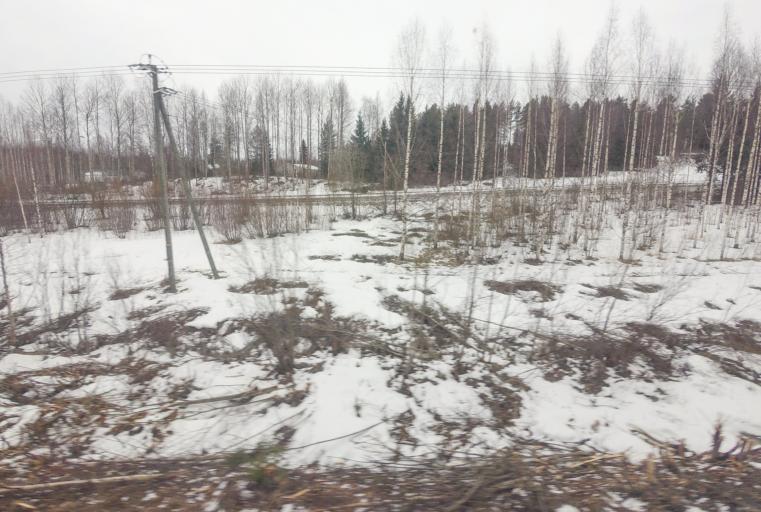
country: FI
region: South Karelia
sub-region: Imatra
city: Parikkala
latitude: 61.5819
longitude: 29.4949
